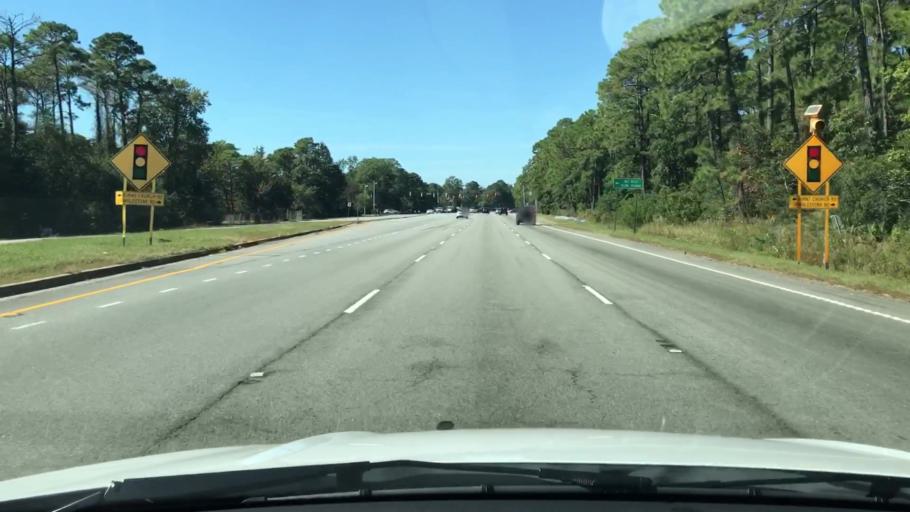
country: US
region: South Carolina
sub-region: Beaufort County
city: Bluffton
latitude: 32.2507
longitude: -80.8400
